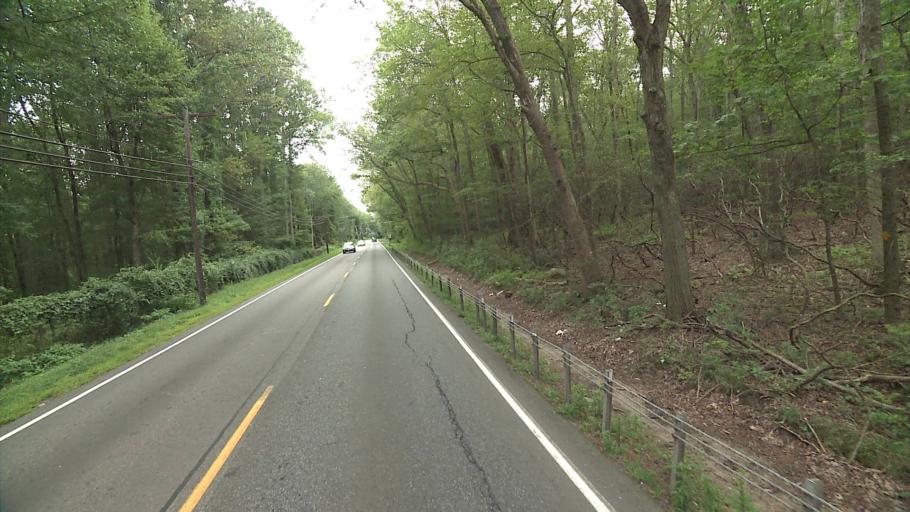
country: US
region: Connecticut
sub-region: New London County
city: Montville Center
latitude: 41.4190
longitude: -72.1955
